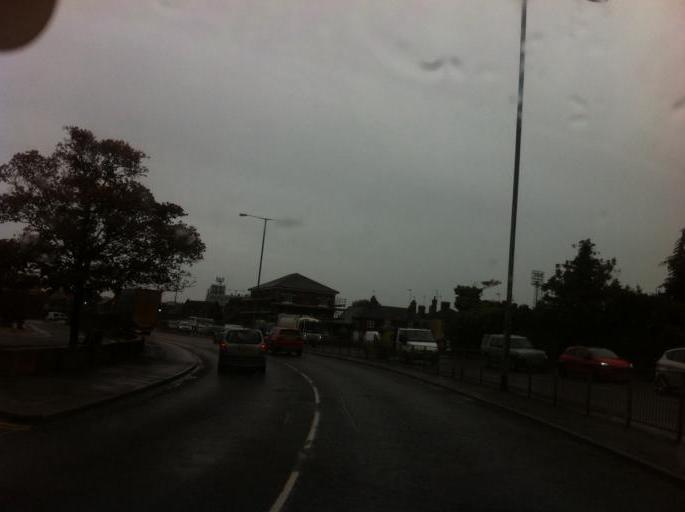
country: GB
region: England
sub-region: Lincolnshire
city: Boston
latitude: 52.9753
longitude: -0.0216
